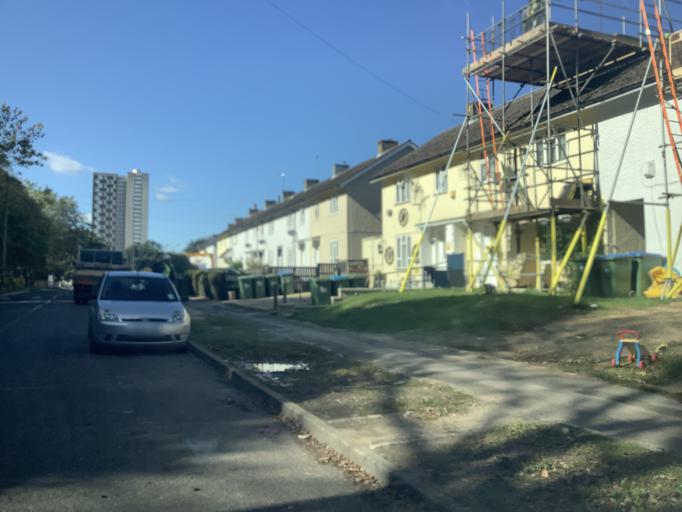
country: GB
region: England
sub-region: Hampshire
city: Totton
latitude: 50.9278
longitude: -1.4545
